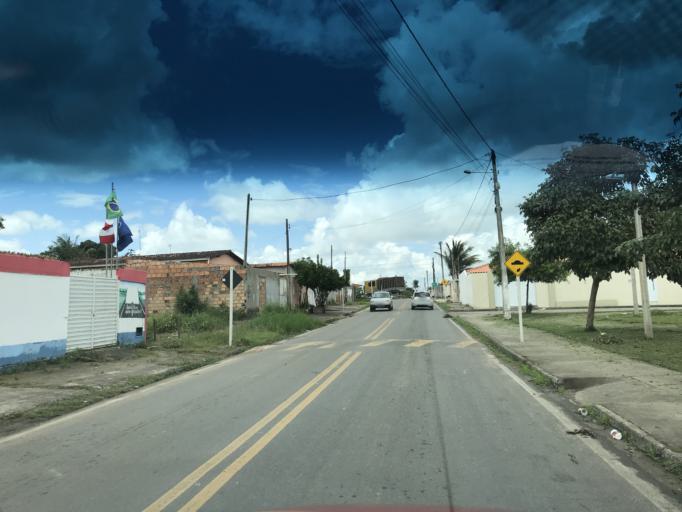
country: BR
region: Bahia
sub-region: Conceicao Do Almeida
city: Conceicao do Almeida
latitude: -12.7363
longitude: -39.1870
